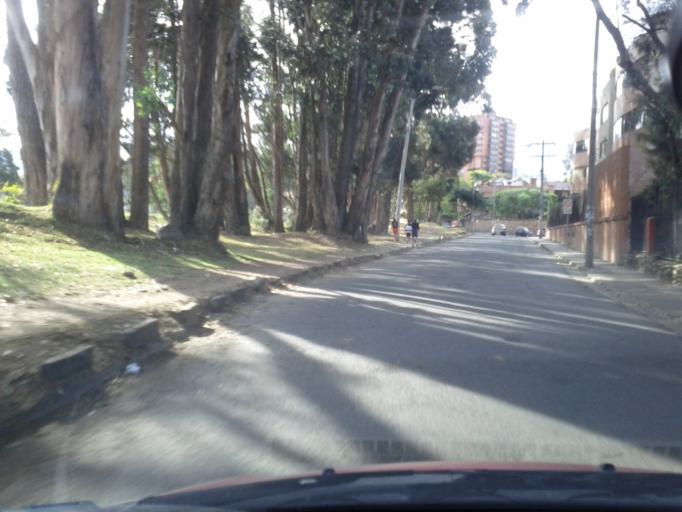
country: EC
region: Azuay
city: Cuenca
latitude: -2.8935
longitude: -79.0264
